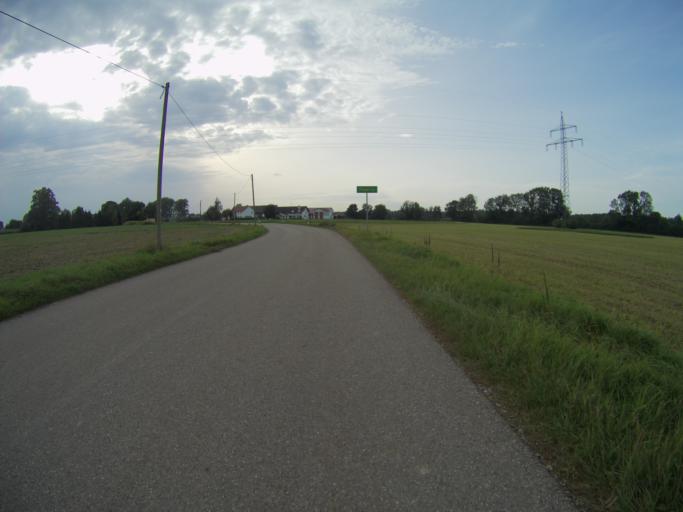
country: DE
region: Bavaria
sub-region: Upper Bavaria
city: Marzling
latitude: 48.3966
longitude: 11.8252
